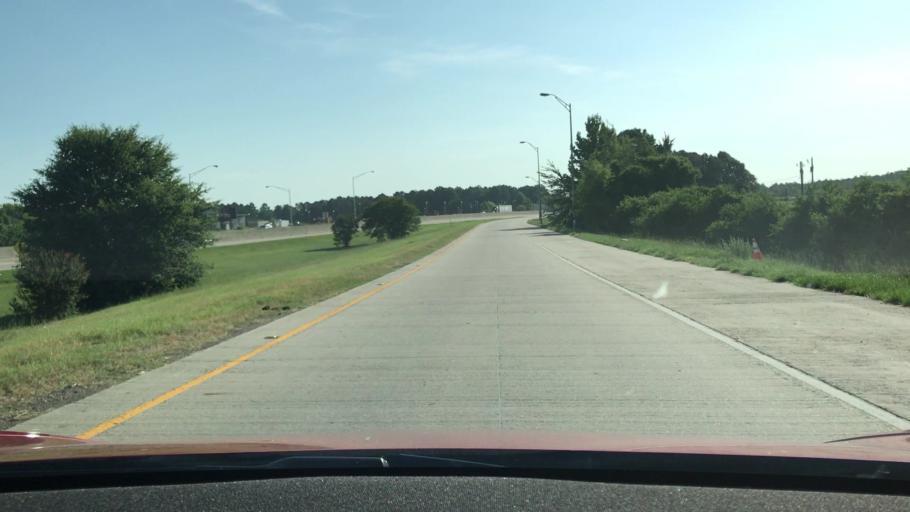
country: US
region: Louisiana
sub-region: Caddo Parish
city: Shreveport
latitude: 32.4559
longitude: -93.8427
